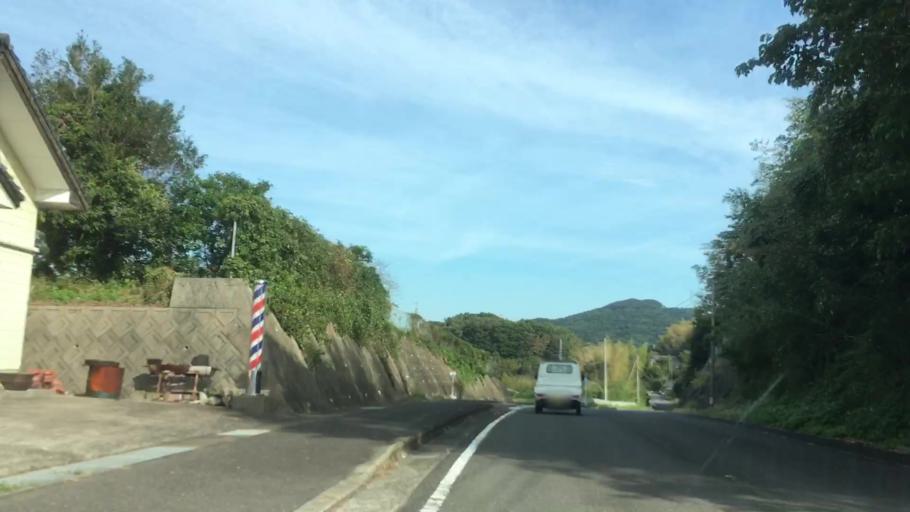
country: JP
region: Nagasaki
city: Sasebo
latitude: 33.0161
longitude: 129.6542
